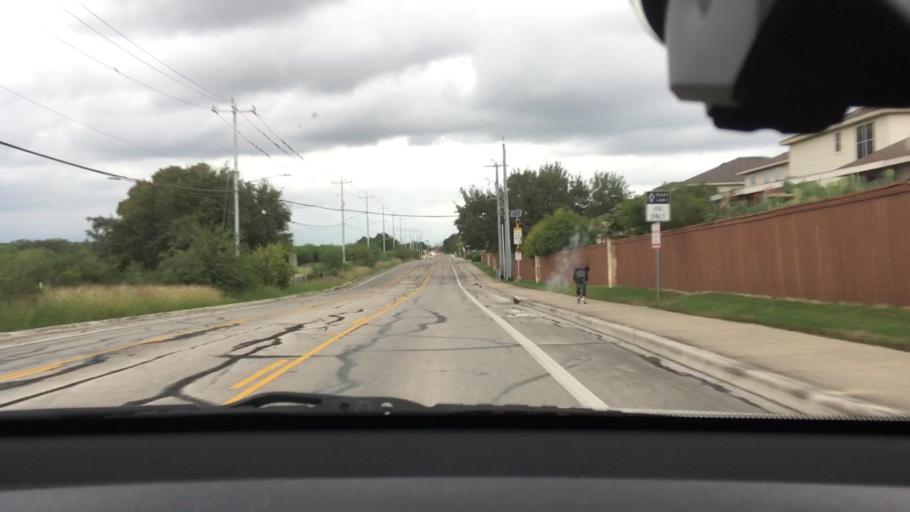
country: US
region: Texas
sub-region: Bexar County
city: Converse
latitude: 29.5312
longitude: -98.3116
